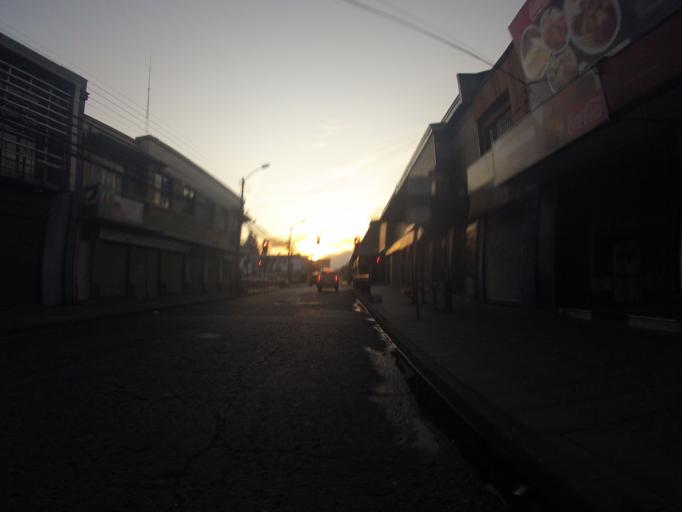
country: CL
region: Araucania
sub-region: Provincia de Cautin
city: Temuco
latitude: -38.7381
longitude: -72.5926
